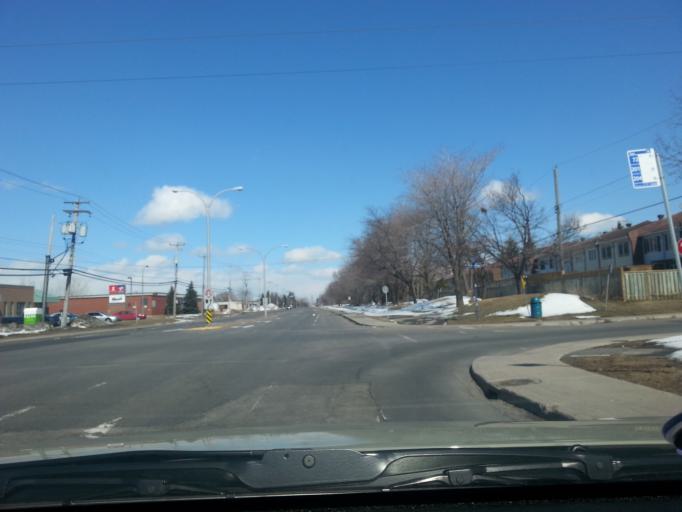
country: CA
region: Quebec
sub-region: Montreal
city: Pointe-Claire
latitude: 45.4613
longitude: -73.8175
